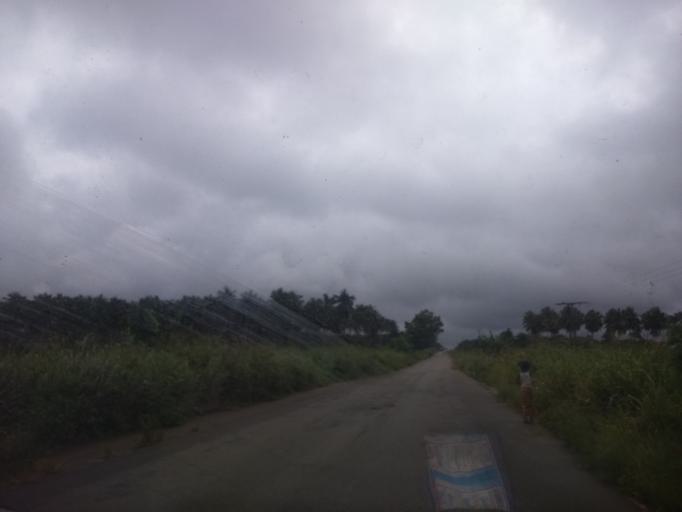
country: CI
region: Sud-Comoe
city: Bonoua
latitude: 5.2883
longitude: -3.4574
